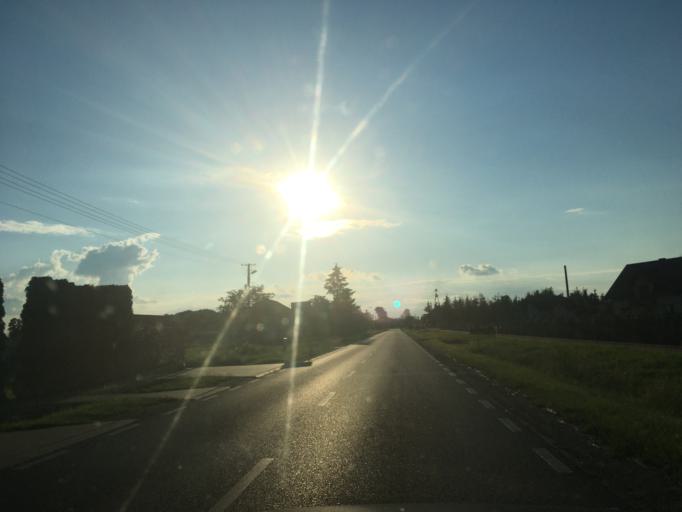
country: PL
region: Masovian Voivodeship
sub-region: Powiat grodziski
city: Grodzisk Mazowiecki
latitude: 52.1179
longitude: 20.5800
